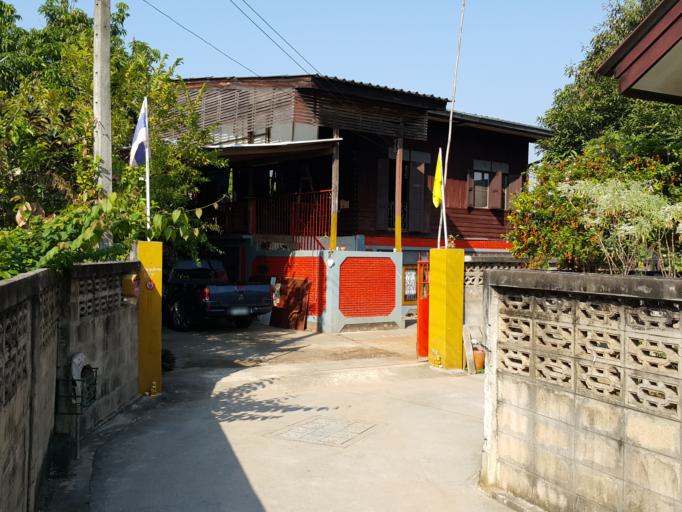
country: TH
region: Lampang
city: Lampang
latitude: 18.2854
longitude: 99.5096
